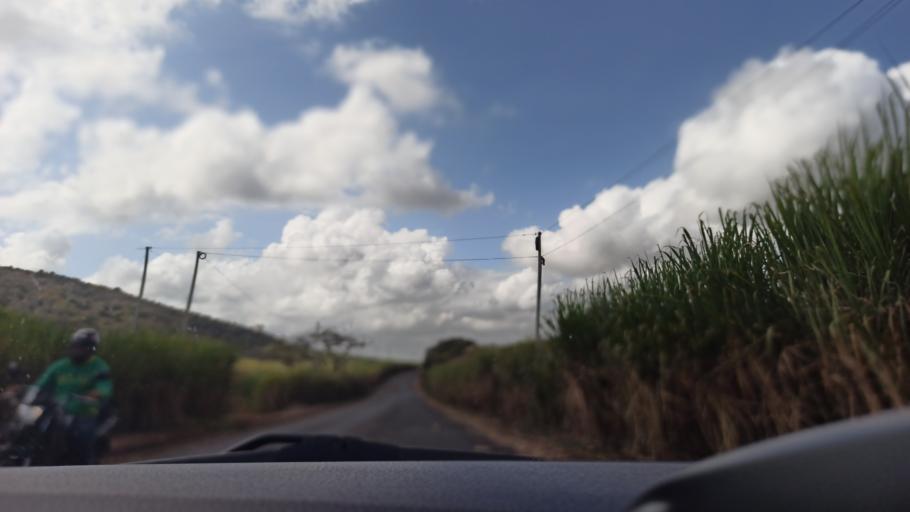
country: BR
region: Paraiba
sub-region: Juripiranga
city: Juripiranga
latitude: -7.3964
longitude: -35.2574
